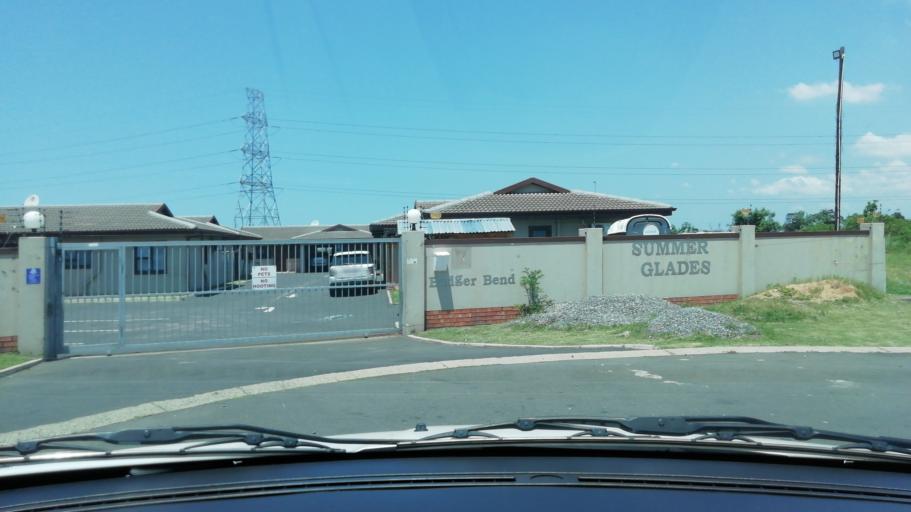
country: ZA
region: KwaZulu-Natal
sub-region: uThungulu District Municipality
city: Richards Bay
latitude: -28.7396
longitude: 32.0482
